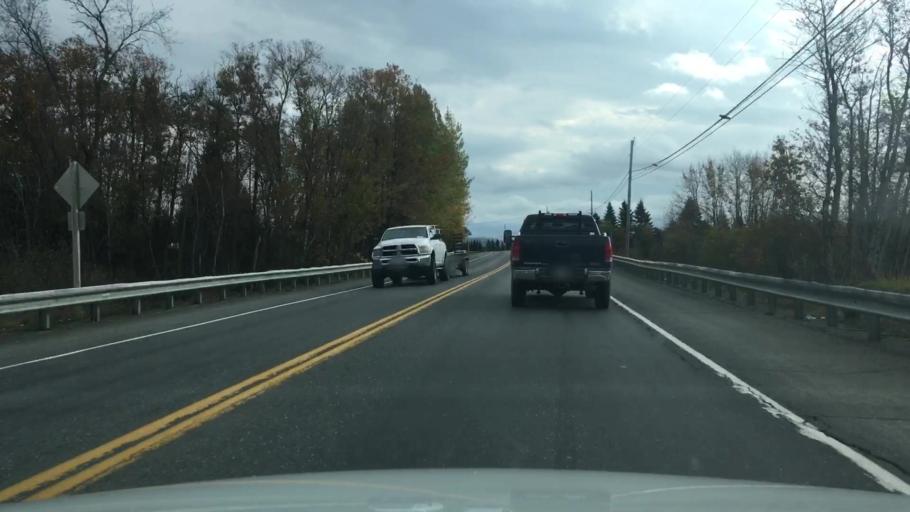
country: US
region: Maine
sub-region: Aroostook County
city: Easton
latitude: 46.5660
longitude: -67.9486
